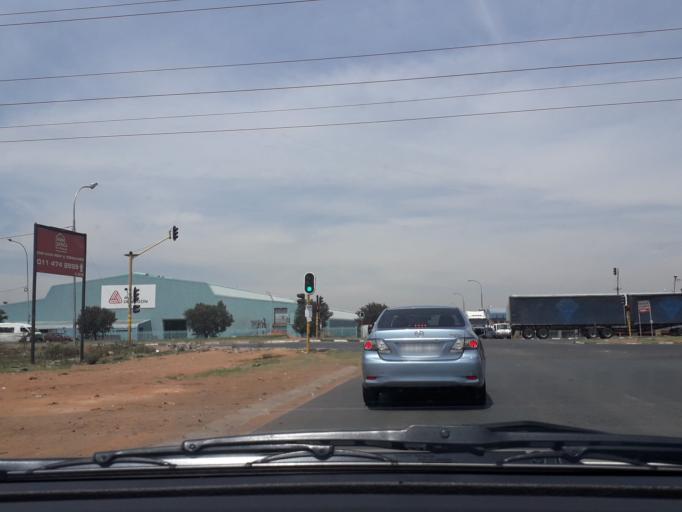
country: ZA
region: Gauteng
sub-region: City of Johannesburg Metropolitan Municipality
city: Roodepoort
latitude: -26.1923
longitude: 27.9231
